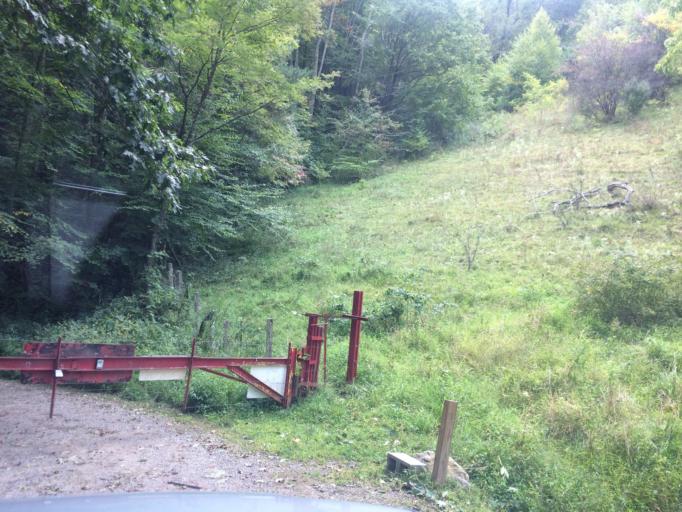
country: US
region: North Carolina
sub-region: Haywood County
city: Clyde
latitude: 35.5570
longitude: -82.9154
